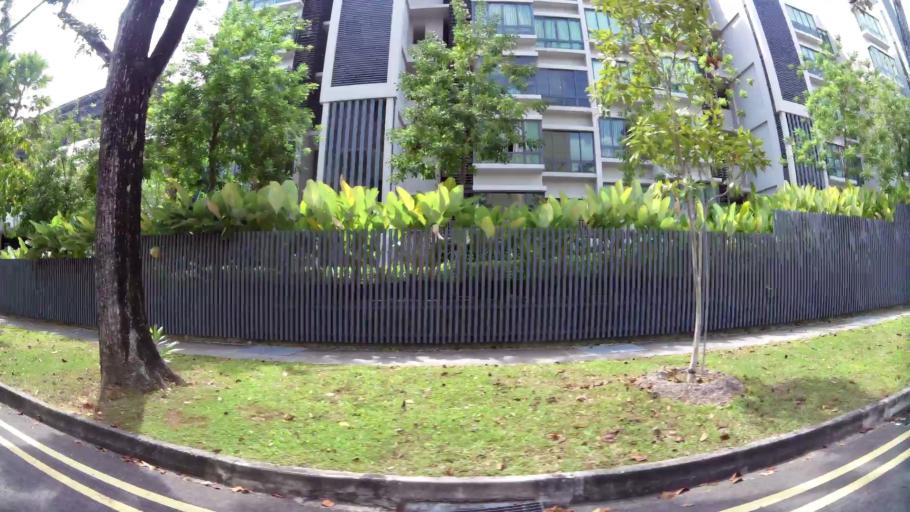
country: SG
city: Singapore
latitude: 1.3396
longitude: 103.7674
